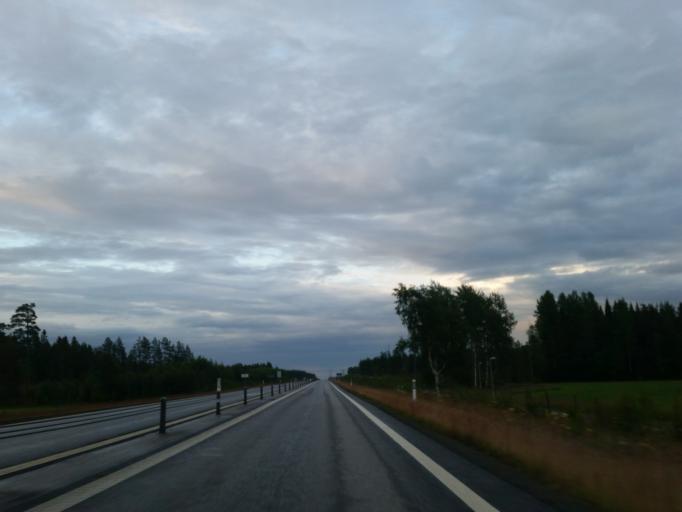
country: SE
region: Vaesterbotten
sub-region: Umea Kommun
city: Ersmark
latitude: 63.8576
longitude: 20.3959
